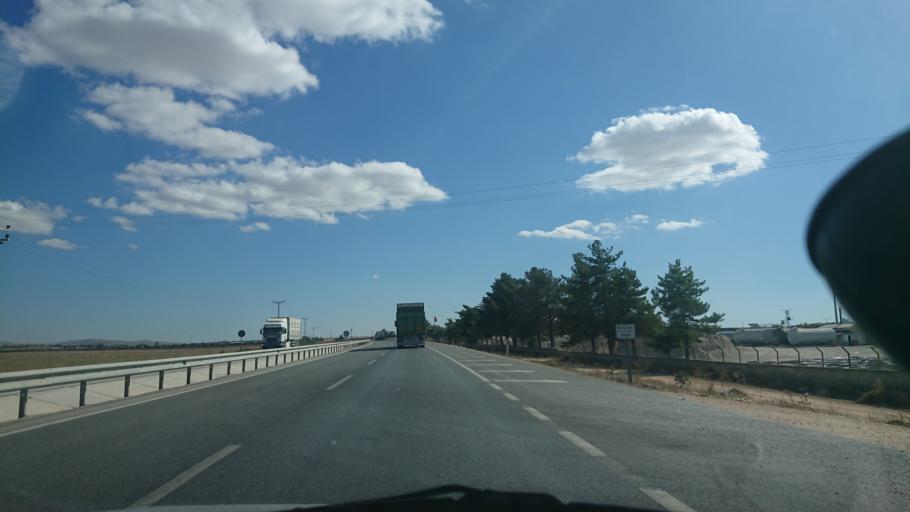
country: TR
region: Eskisehir
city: Mahmudiye
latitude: 39.5628
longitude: 30.9153
